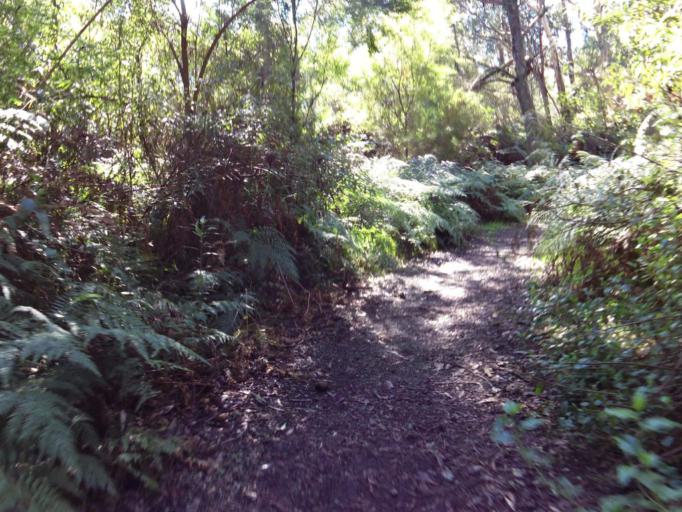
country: AU
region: Victoria
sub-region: Baw Baw
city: Warragul
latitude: -38.0535
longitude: 145.9644
